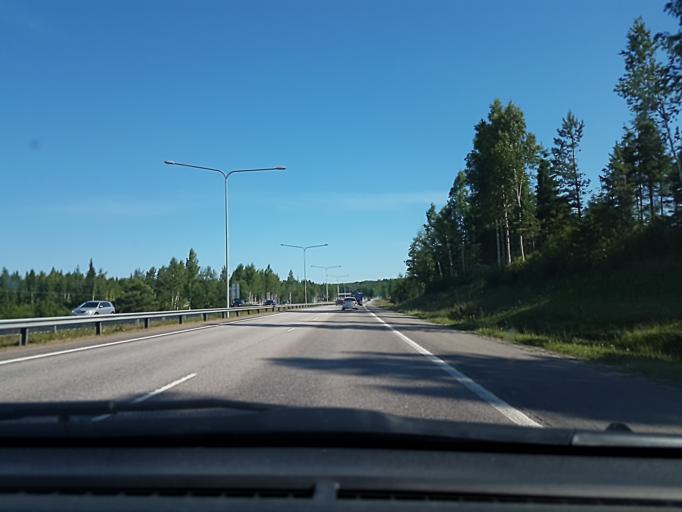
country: FI
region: Uusimaa
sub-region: Helsinki
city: Vantaa
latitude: 60.3342
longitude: 24.9996
